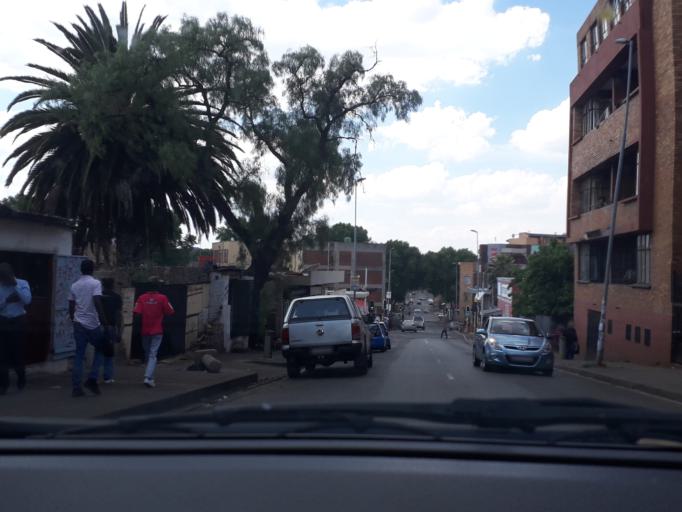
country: ZA
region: Gauteng
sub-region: City of Johannesburg Metropolitan Municipality
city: Johannesburg
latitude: -26.1819
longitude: 28.0681
